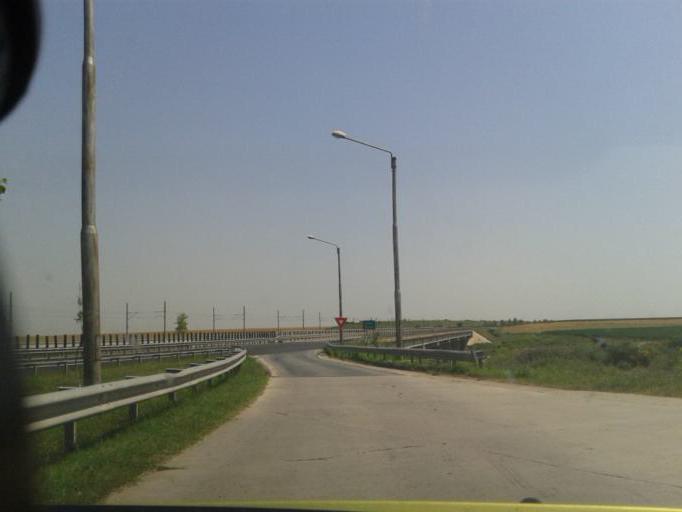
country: RO
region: Calarasi
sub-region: Comuna Sarulesti
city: Sarulesti-Gara
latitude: 44.4428
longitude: 26.6814
